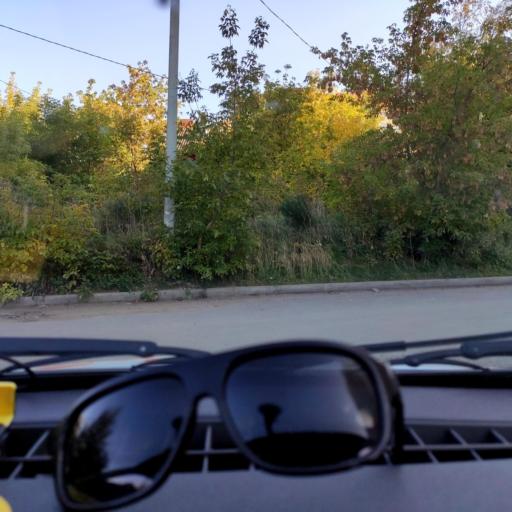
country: RU
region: Bashkortostan
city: Ufa
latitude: 54.7050
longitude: 55.9794
